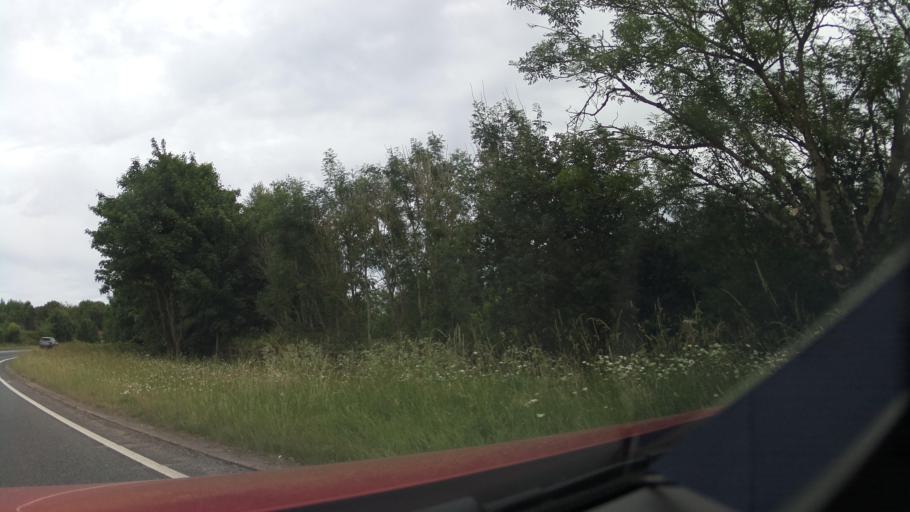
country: GB
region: England
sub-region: Devon
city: Ashburton
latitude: 50.5346
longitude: -3.7176
